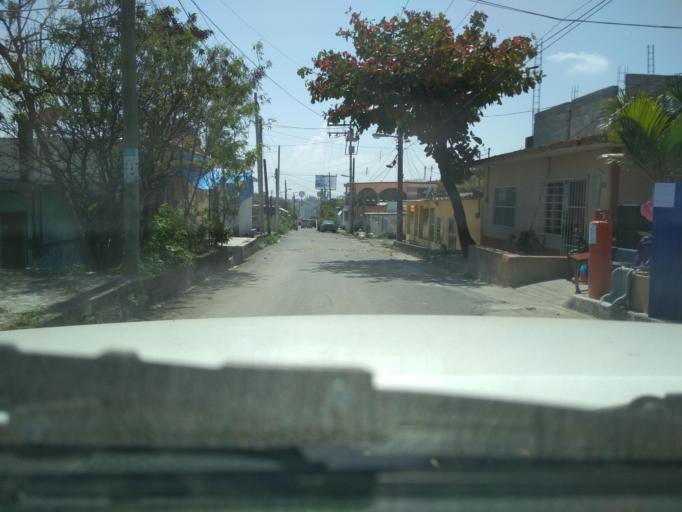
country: MX
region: Veracruz
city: Veracruz
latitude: 19.1666
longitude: -96.1382
